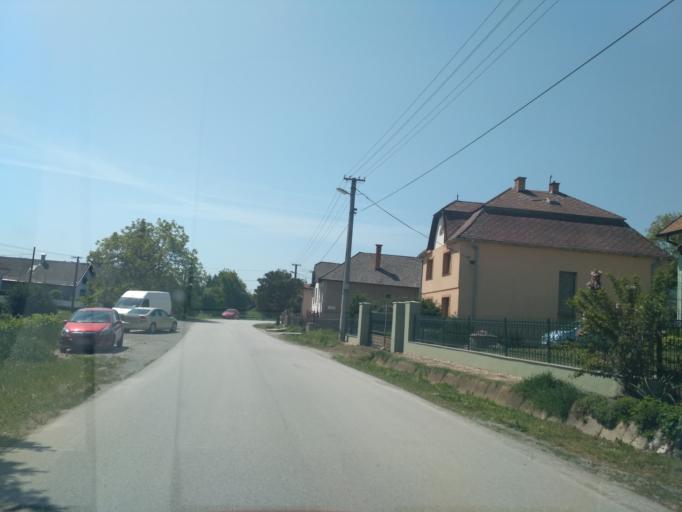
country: SK
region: Kosicky
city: Kosice
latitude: 48.7935
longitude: 21.3512
